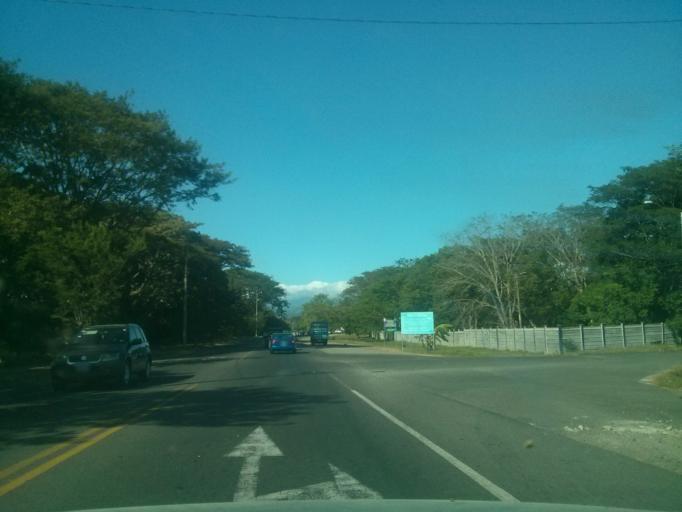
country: CR
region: Puntarenas
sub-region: Canton Central de Puntarenas
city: Chacarita
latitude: 9.9801
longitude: -84.7399
